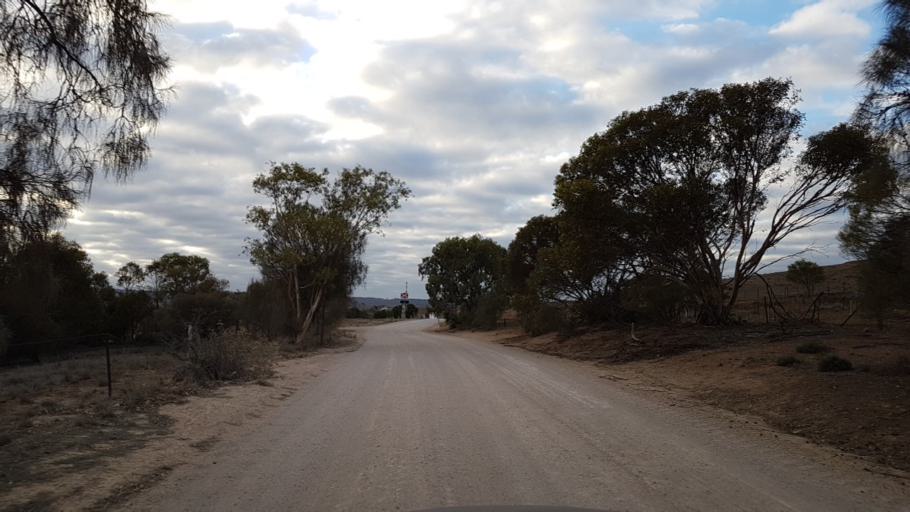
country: AU
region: South Australia
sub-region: Mount Barker
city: Callington
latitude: -35.1054
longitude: 139.0095
